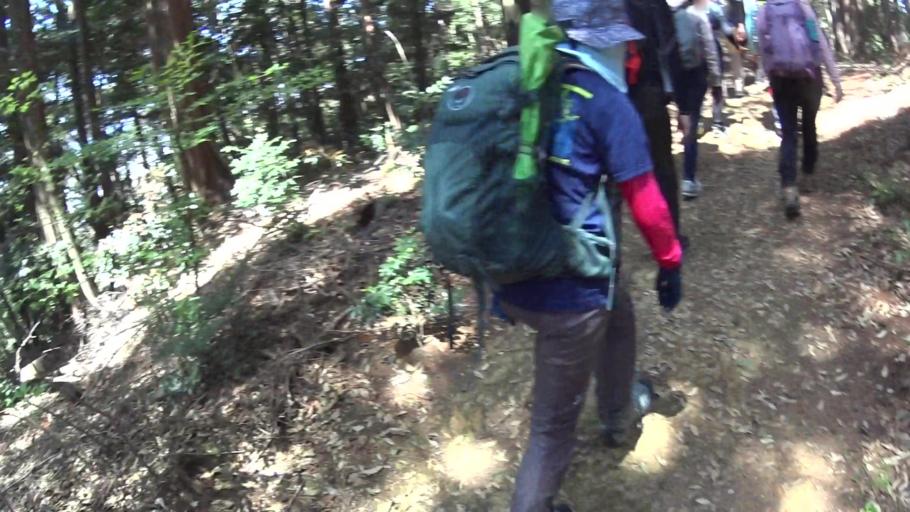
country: JP
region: Kyoto
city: Kyoto
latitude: 34.9962
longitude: 135.7874
